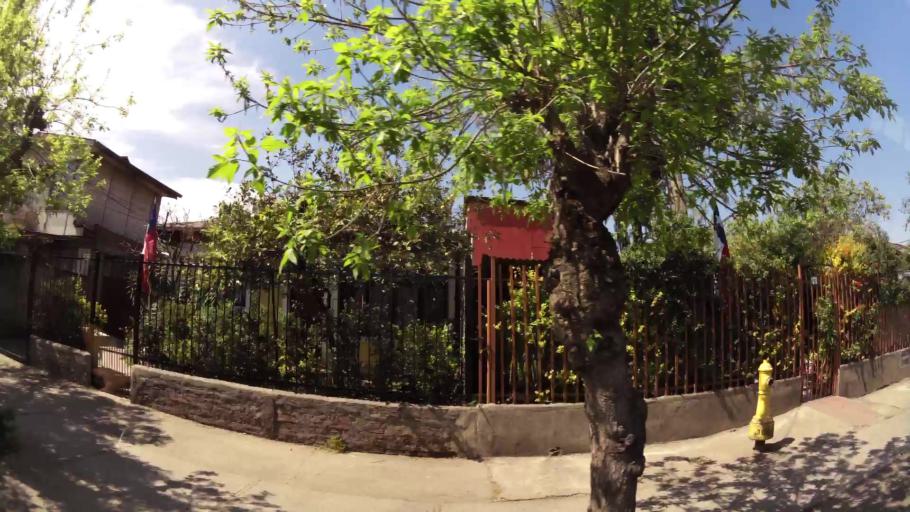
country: CL
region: Santiago Metropolitan
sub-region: Provincia de Santiago
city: Villa Presidente Frei, Nunoa, Santiago, Chile
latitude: -33.4701
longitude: -70.5411
